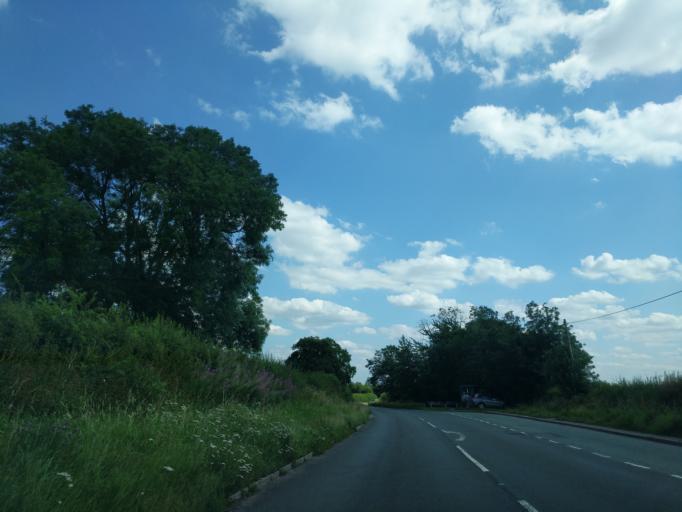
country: GB
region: England
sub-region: Staffordshire
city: Uttoxeter
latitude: 52.9309
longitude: -1.9244
